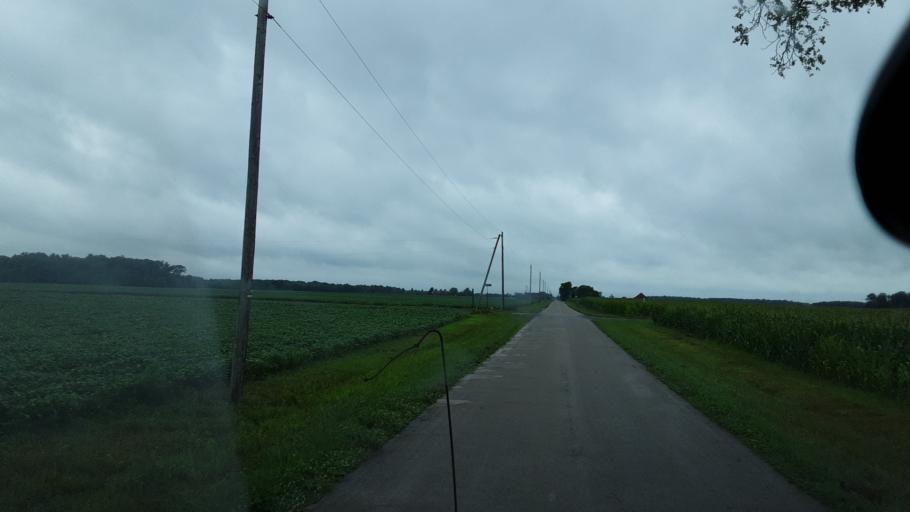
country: US
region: Ohio
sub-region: Van Wert County
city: Convoy
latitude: 40.8296
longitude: -84.7593
